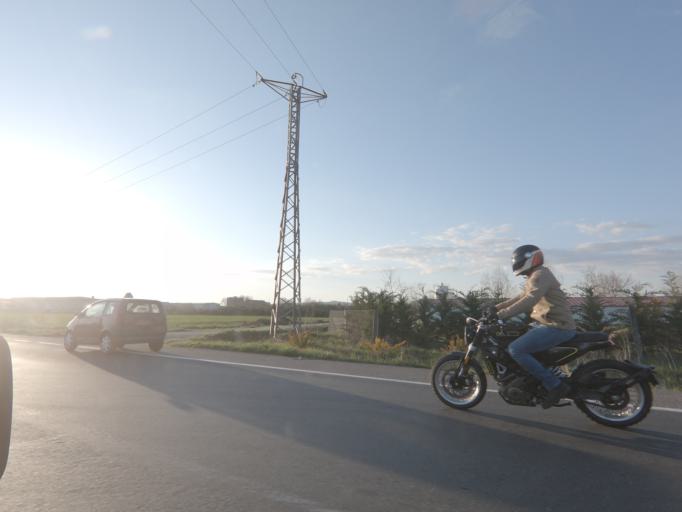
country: ES
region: Galicia
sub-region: Provincia de Ourense
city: Xinzo de Limia
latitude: 42.0785
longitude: -7.7162
